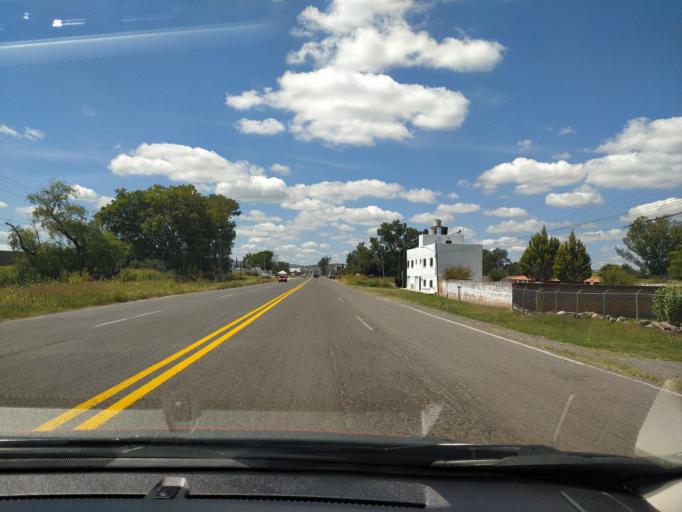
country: MX
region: Jalisco
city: San Miguel el Alto
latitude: 21.0267
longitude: -102.3769
